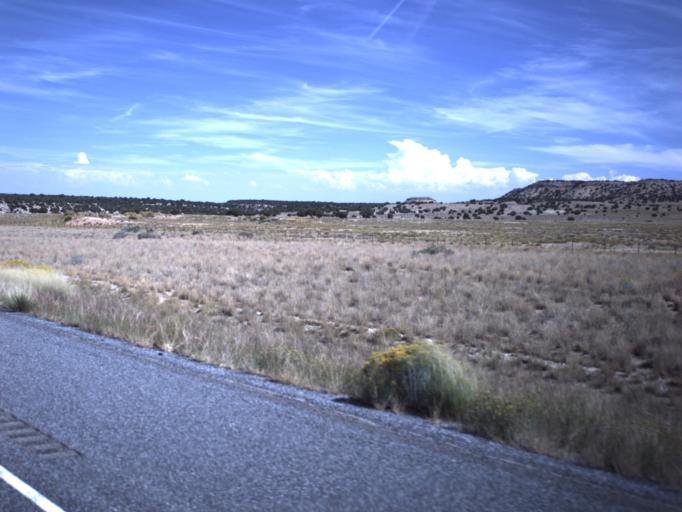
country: US
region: Utah
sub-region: Emery County
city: Castle Dale
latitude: 38.9022
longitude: -110.5633
